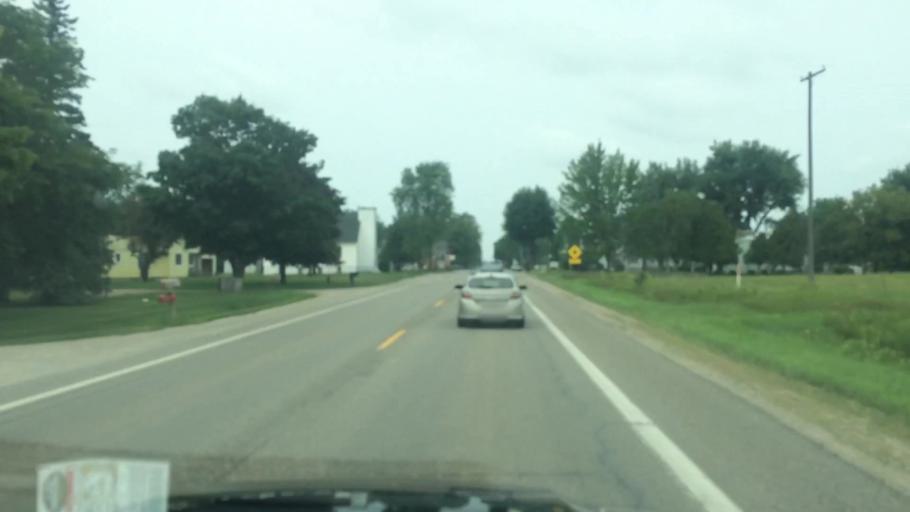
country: US
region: Michigan
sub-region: Huron County
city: Bad Axe
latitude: 43.8934
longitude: -83.0033
